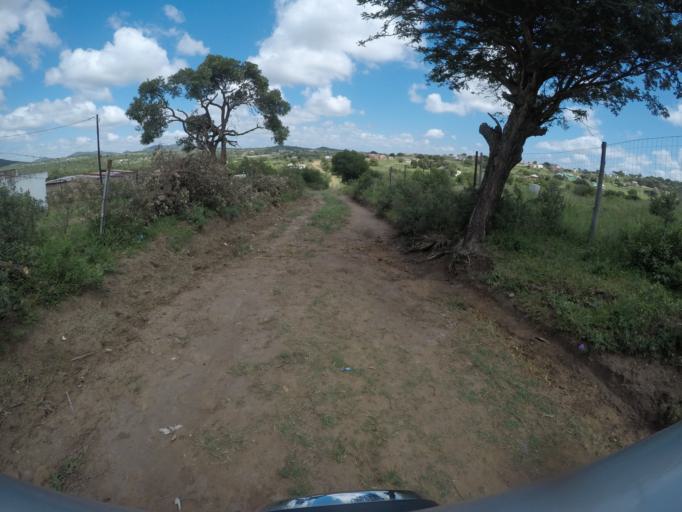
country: ZA
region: KwaZulu-Natal
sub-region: uThungulu District Municipality
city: Empangeni
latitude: -28.5837
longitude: 31.8429
